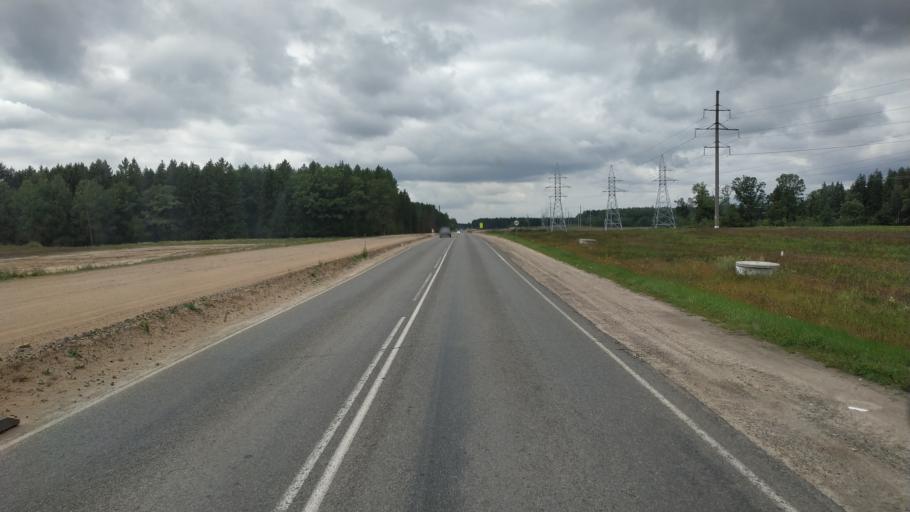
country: BY
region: Mogilev
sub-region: Mahilyowski Rayon
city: Kadino
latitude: 53.8727
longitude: 30.4471
